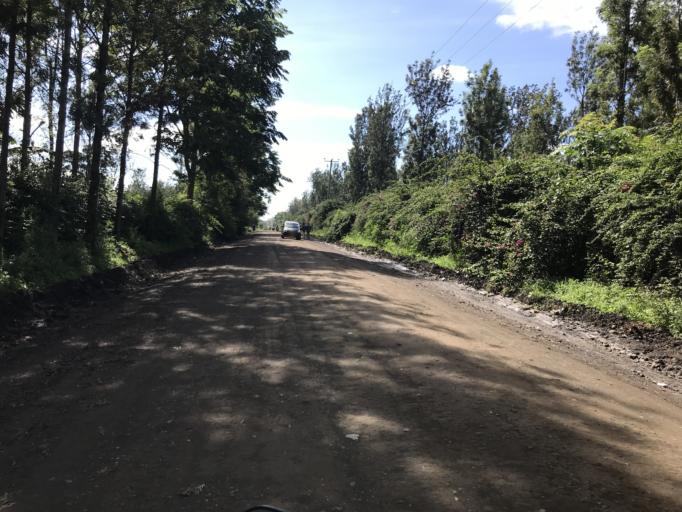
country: TZ
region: Arusha
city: Nkoaranga
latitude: -3.3775
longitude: 36.7902
